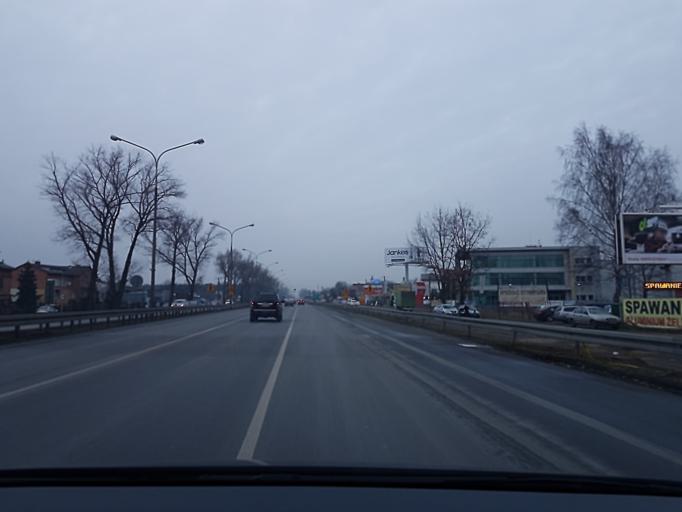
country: PL
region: Masovian Voivodeship
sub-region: Powiat wolominski
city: Marki
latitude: 52.3099
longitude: 21.0945
